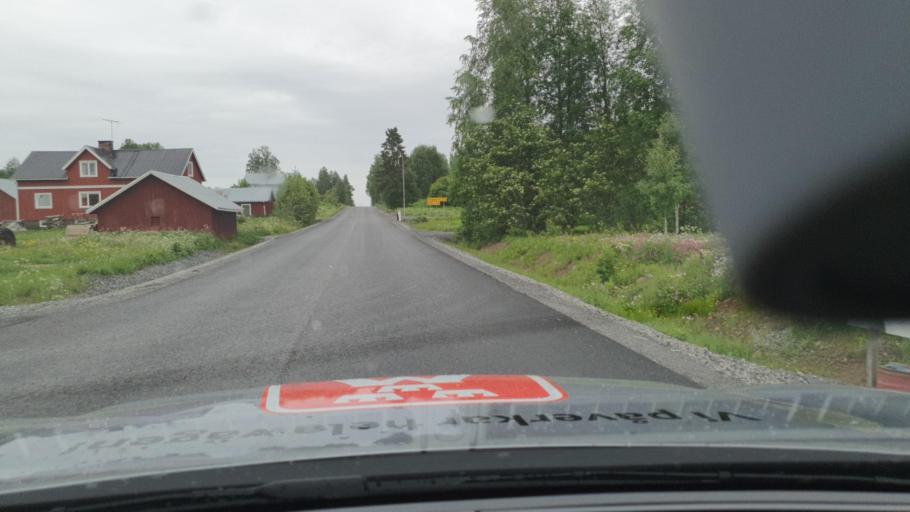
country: SE
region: Norrbotten
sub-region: Pajala Kommun
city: Pajala
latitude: 66.7294
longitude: 23.1784
